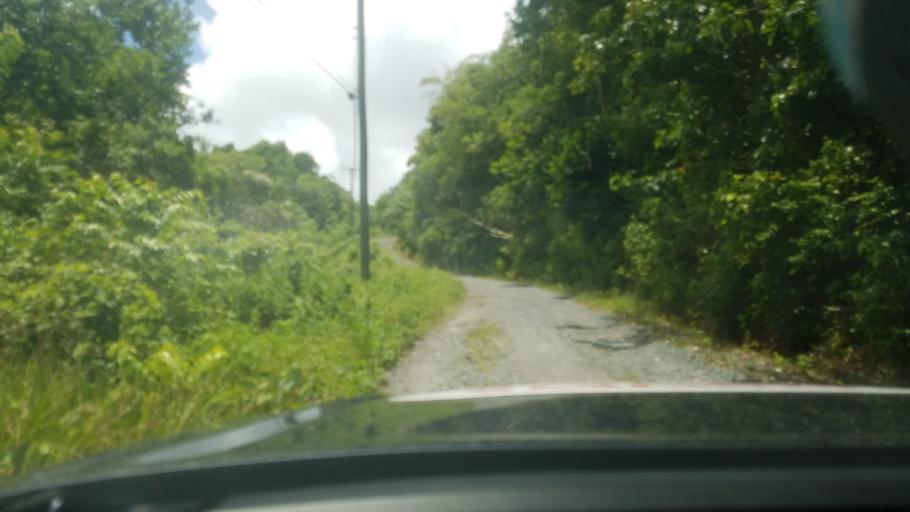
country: LC
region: Praslin
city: Praslin
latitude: 13.8679
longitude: -60.9146
